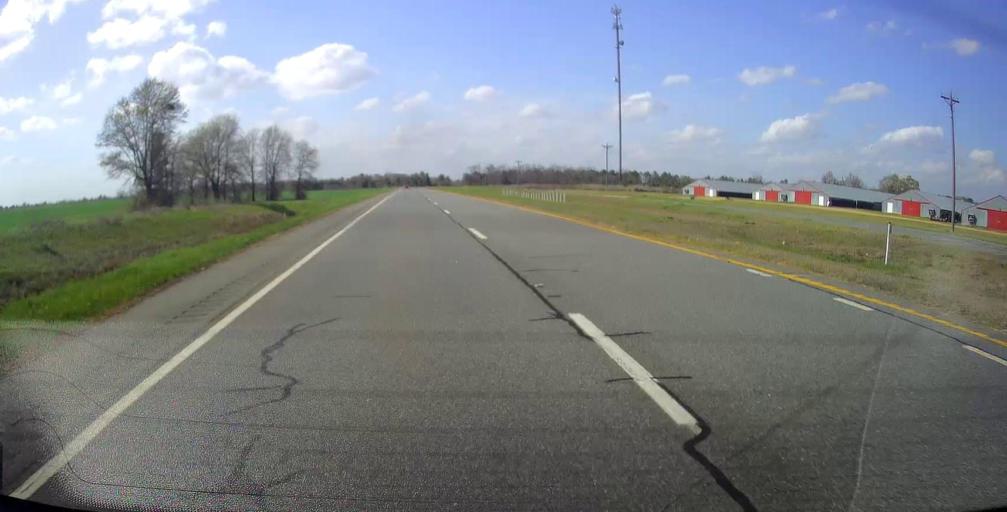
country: US
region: Georgia
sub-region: Pulaski County
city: Hawkinsville
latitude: 32.2452
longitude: -83.3815
